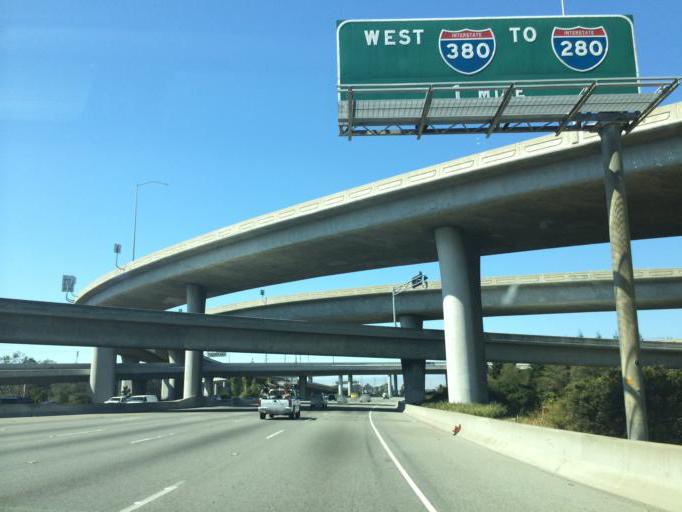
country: US
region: California
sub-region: San Mateo County
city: Millbrae
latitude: 37.6133
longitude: -122.3960
